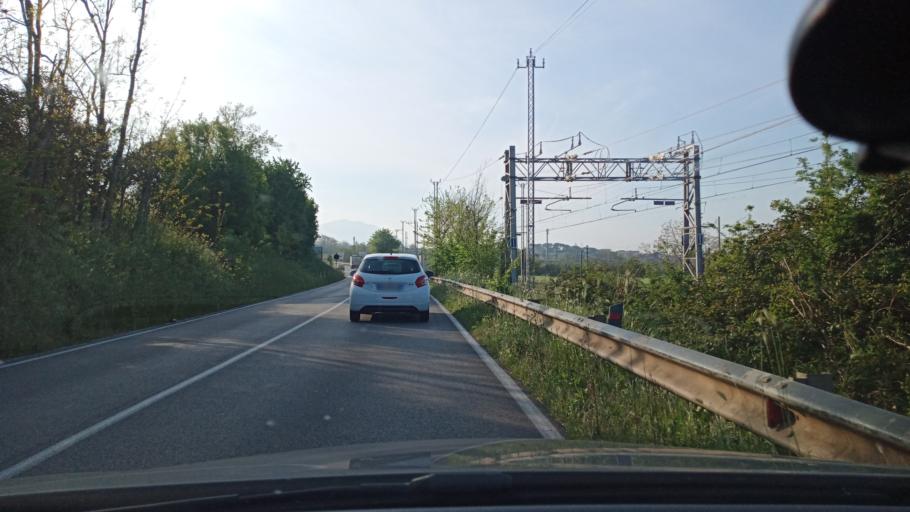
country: IT
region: Latium
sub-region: Citta metropolitana di Roma Capitale
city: Fiano Romano
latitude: 42.1648
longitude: 12.6435
